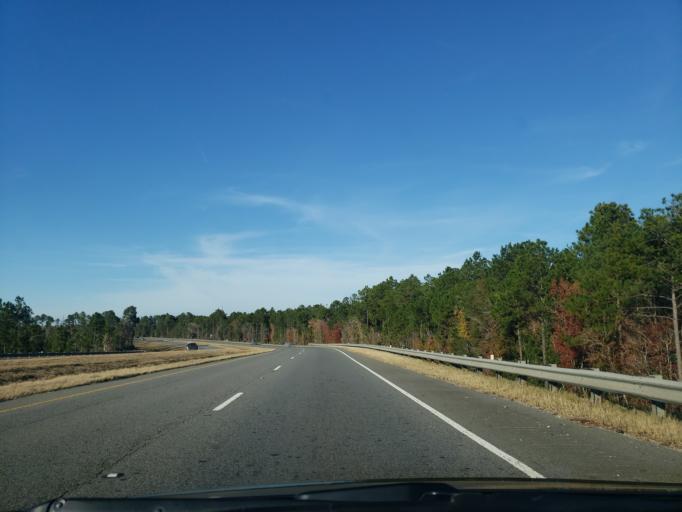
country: US
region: Georgia
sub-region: Ware County
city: Deenwood
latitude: 31.2357
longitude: -82.4267
